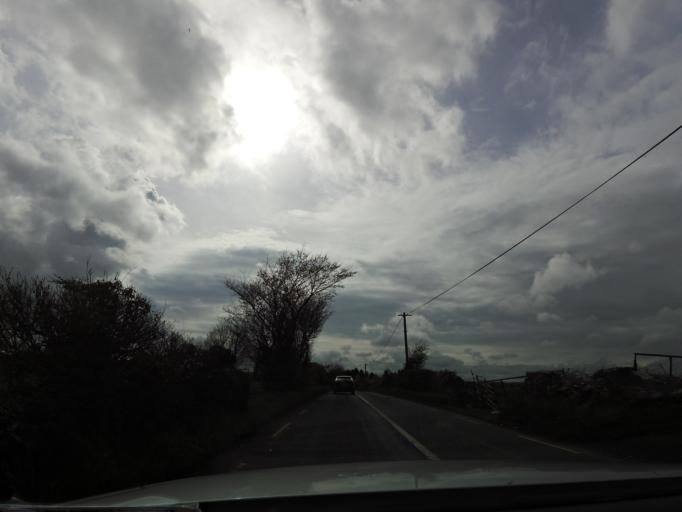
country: IE
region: Leinster
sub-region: Laois
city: Rathdowney
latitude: 52.7242
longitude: -7.5467
